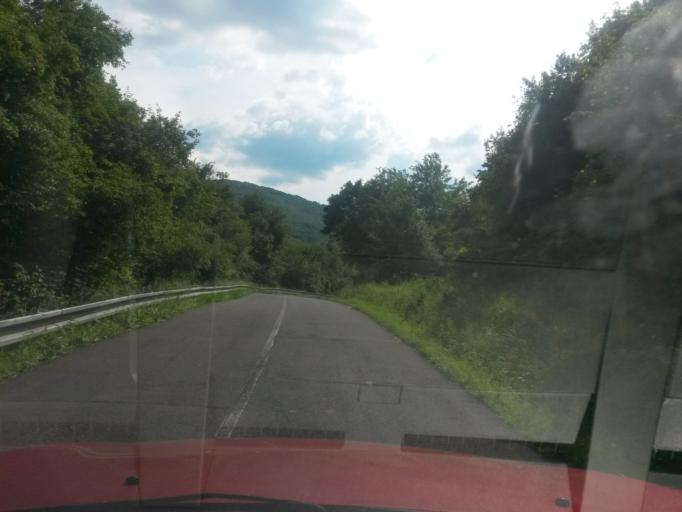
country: SK
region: Presovsky
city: Snina
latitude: 49.1269
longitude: 22.1011
